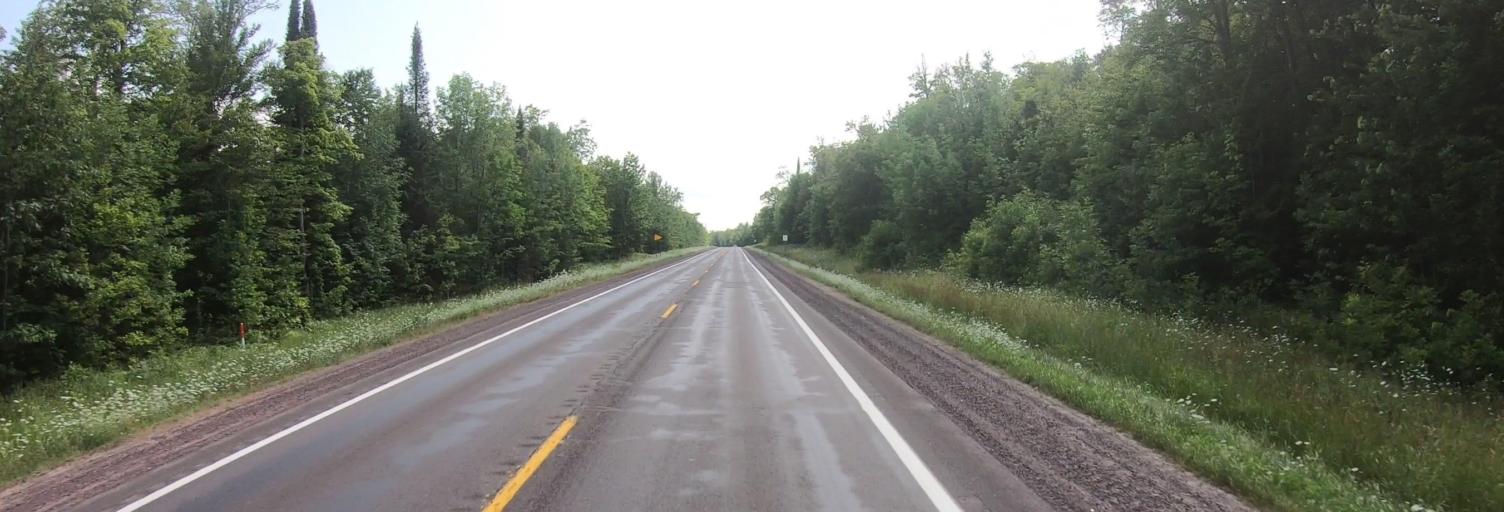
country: US
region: Michigan
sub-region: Ontonagon County
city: Ontonagon
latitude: 46.8346
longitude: -88.9938
